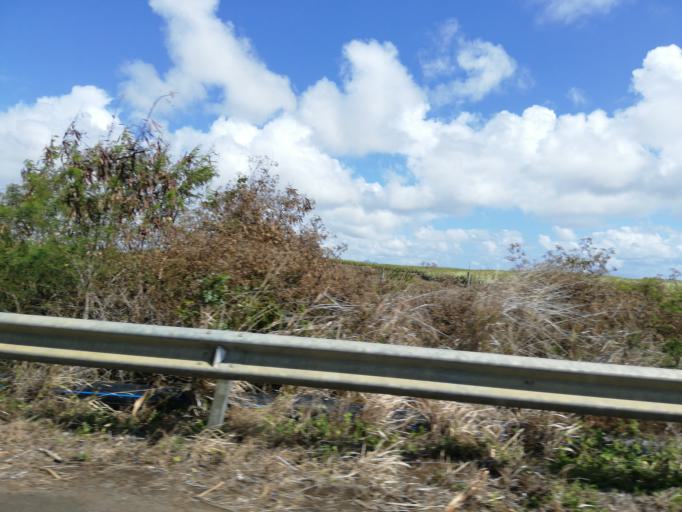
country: MU
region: Riviere du Rempart
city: Goodlands
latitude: -20.0377
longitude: 57.6328
